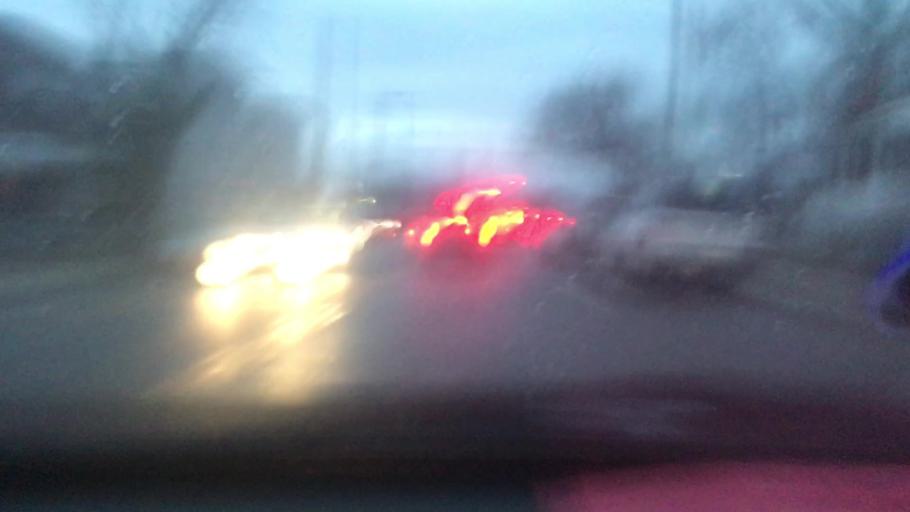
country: US
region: Maryland
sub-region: Prince George's County
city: Seat Pleasant
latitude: 38.8932
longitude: -76.9109
